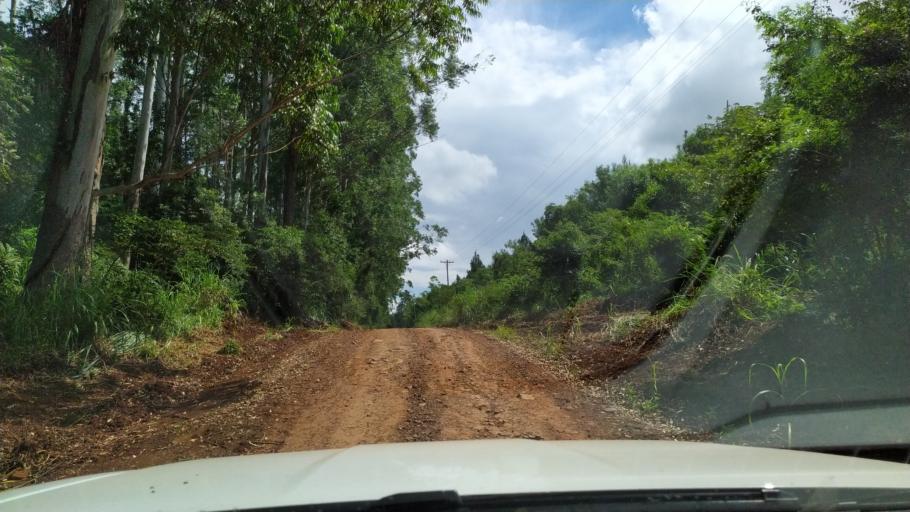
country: AR
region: Misiones
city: Puerto Piray
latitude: -26.5324
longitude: -54.6166
